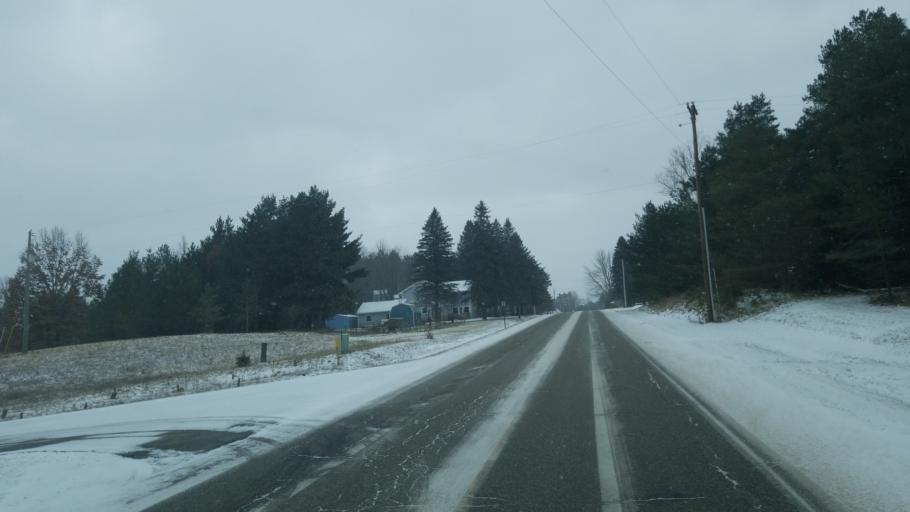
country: US
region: Michigan
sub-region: Osceola County
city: Evart
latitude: 43.9117
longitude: -85.2567
